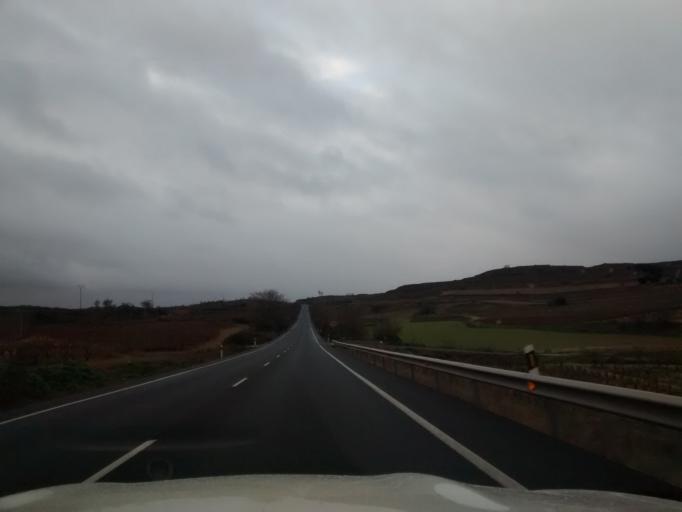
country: ES
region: La Rioja
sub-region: Provincia de La Rioja
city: Torremontalbo
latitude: 42.5087
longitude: -2.7067
